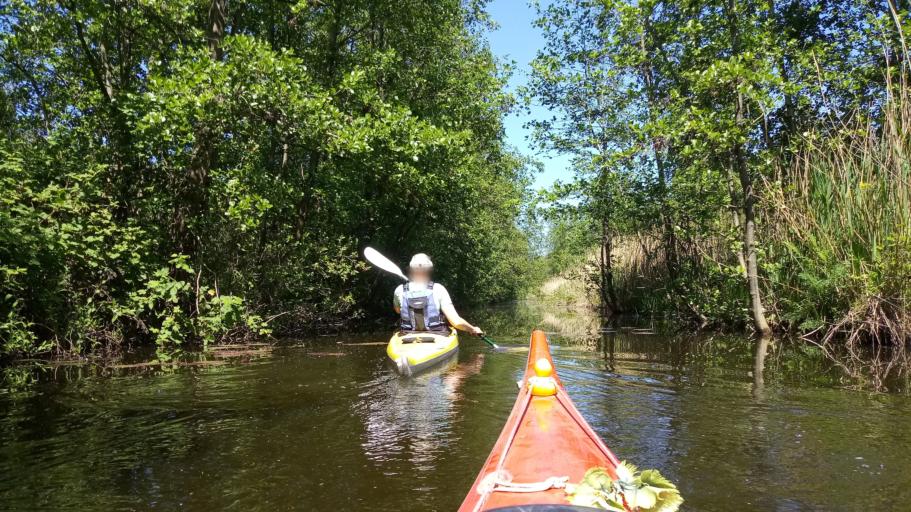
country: NL
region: South Holland
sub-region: Gemeente Nieuwkoop
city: Nieuwkoop
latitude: 52.1590
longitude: 4.8179
